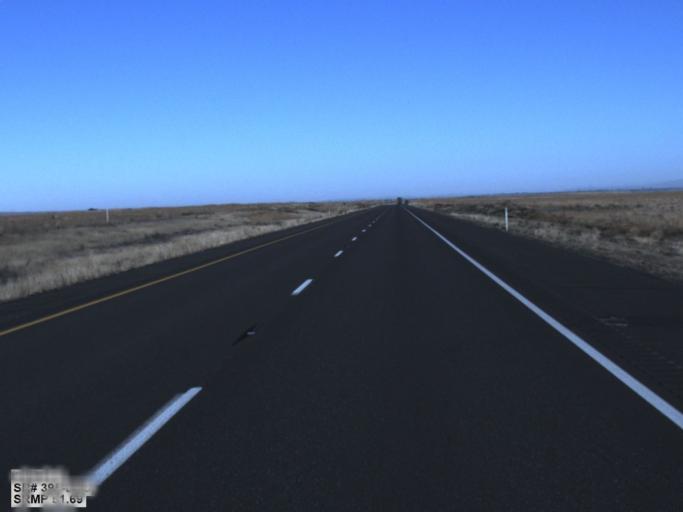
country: US
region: Washington
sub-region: Franklin County
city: Connell
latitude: 46.6193
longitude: -118.8995
